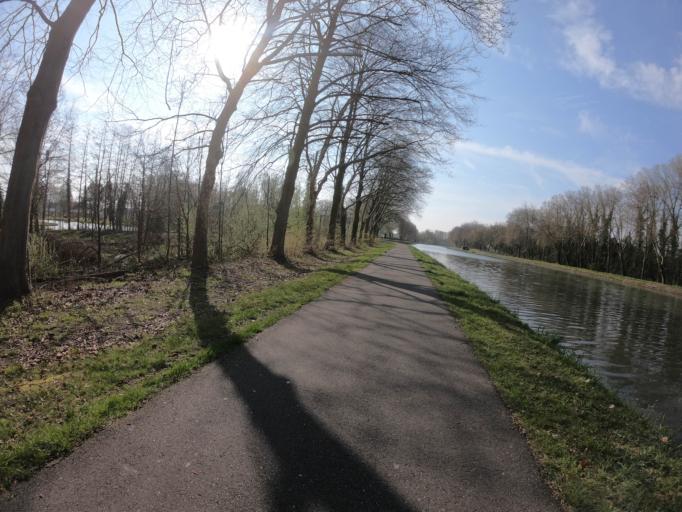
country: BE
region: Flanders
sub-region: Provincie Limburg
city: Kinrooi
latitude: 51.0844
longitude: 5.6979
